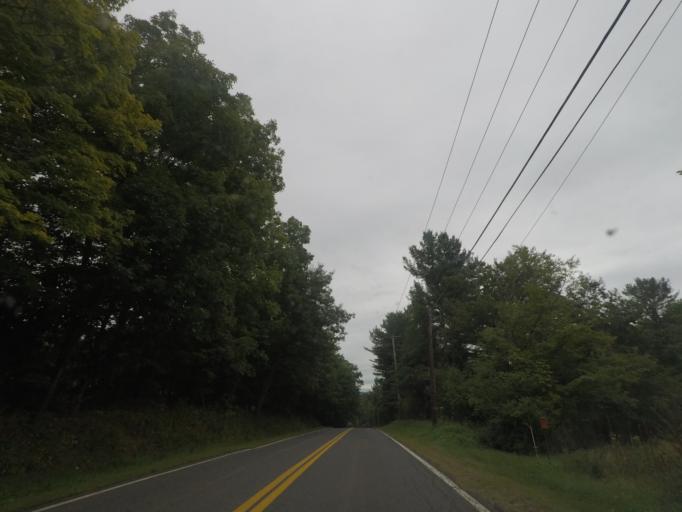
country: US
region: New York
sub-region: Columbia County
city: Chatham
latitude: 42.4167
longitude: -73.5390
